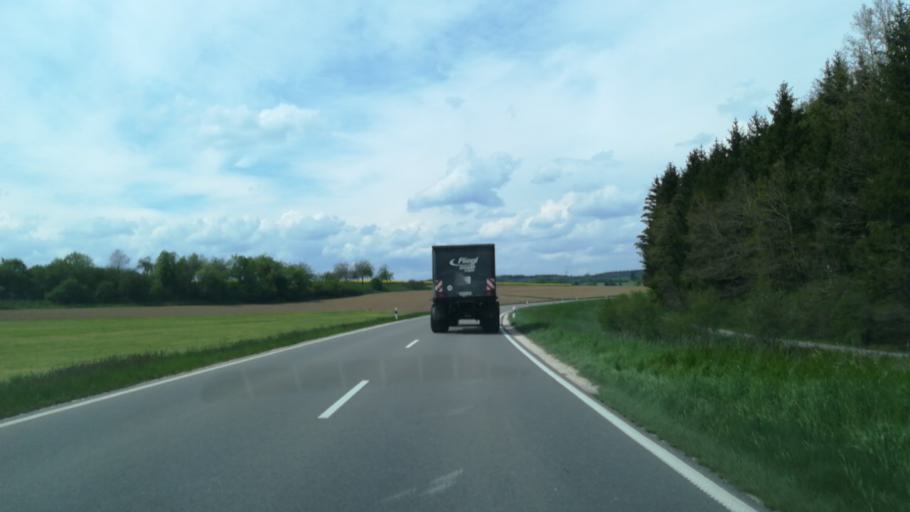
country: DE
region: Baden-Wuerttemberg
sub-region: Tuebingen Region
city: Messkirch
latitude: 48.0124
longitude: 9.1124
